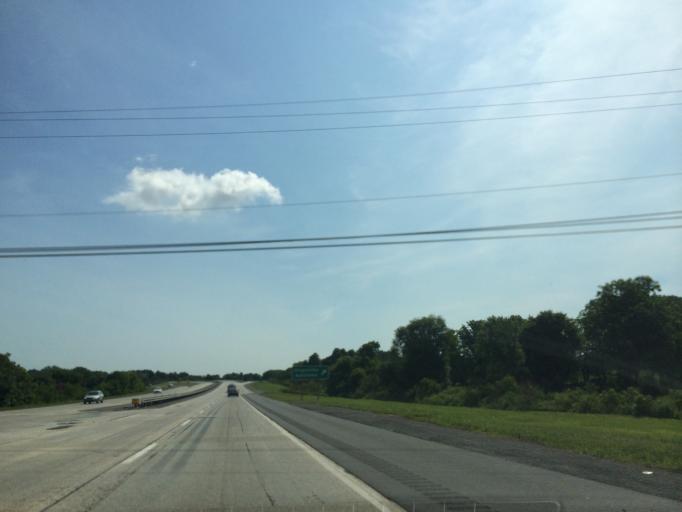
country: US
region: Pennsylvania
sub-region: Berks County
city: Fleetwood
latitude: 40.4943
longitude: -75.8157
